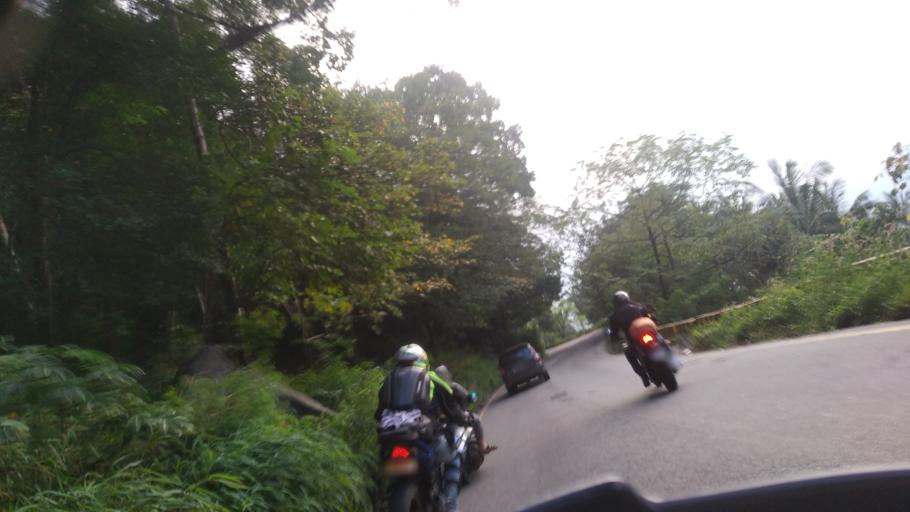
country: IN
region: Kerala
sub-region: Wayanad
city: Kalpetta
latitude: 11.4986
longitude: 76.0222
